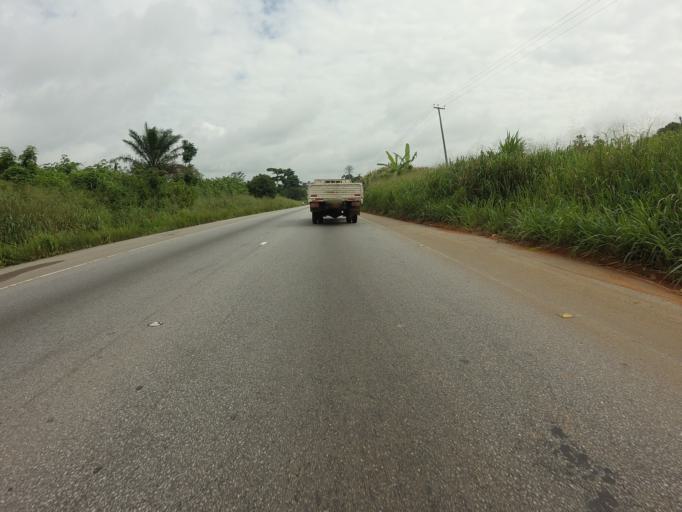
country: GH
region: Ashanti
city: Tafo
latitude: 6.9863
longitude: -1.6895
